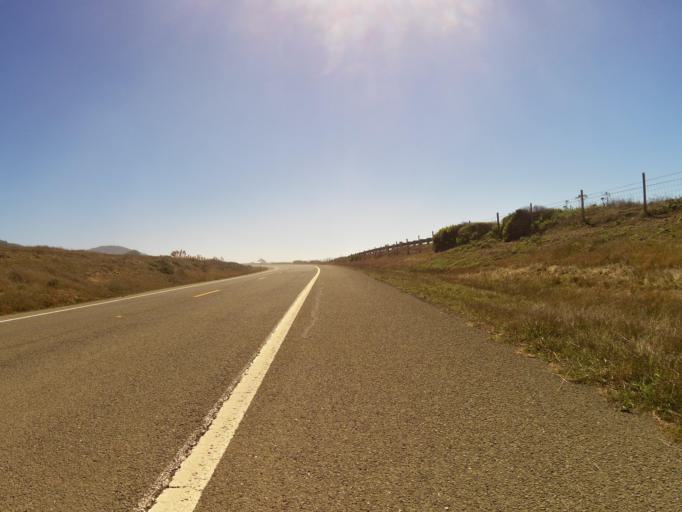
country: US
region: California
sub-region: Mendocino County
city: Fort Bragg
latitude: 39.6736
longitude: -123.7906
